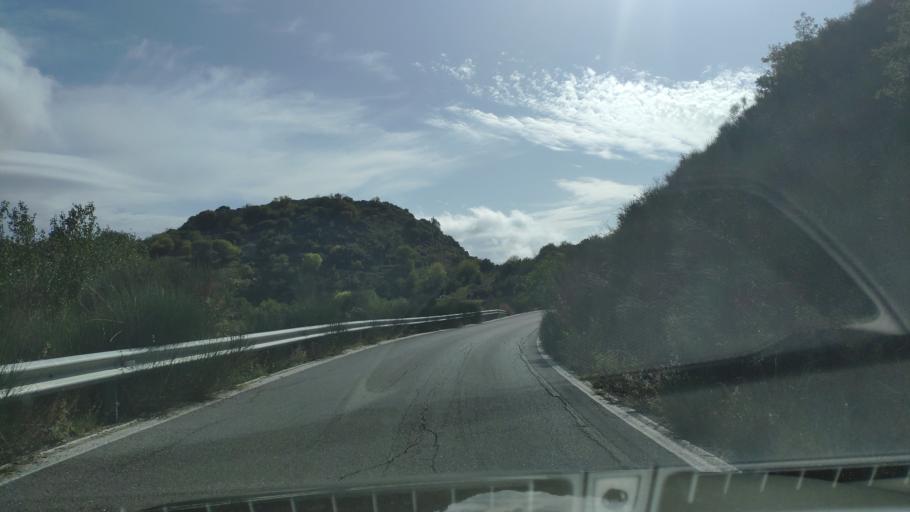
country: GR
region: Peloponnese
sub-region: Nomos Arkadias
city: Dimitsana
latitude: 37.5806
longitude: 22.0171
